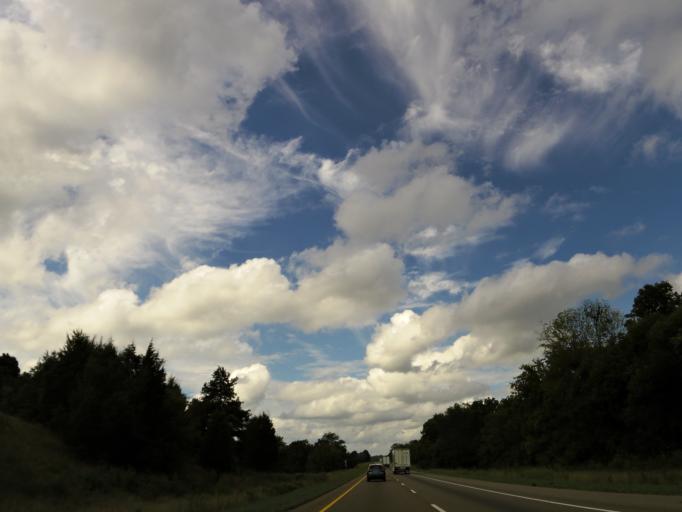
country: US
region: Tennessee
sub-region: Loudon County
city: Loudon
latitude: 35.7922
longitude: -84.3292
